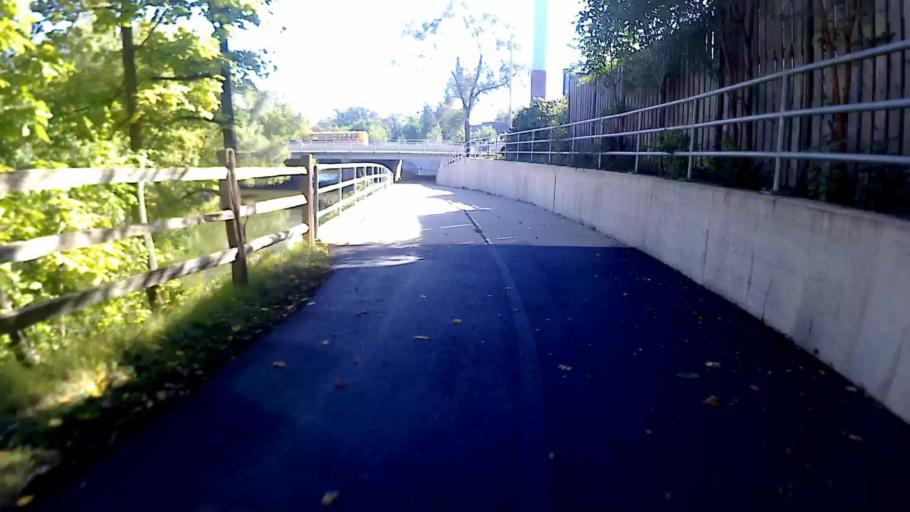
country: US
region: Illinois
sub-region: DuPage County
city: Villa Park
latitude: 41.9064
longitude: -87.9684
